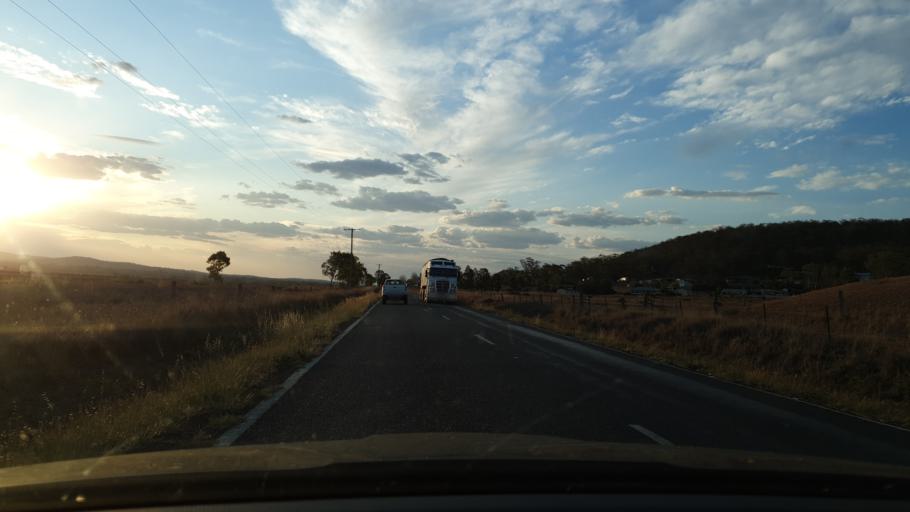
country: AU
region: Queensland
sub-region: Southern Downs
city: Warwick
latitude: -28.1850
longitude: 152.0011
